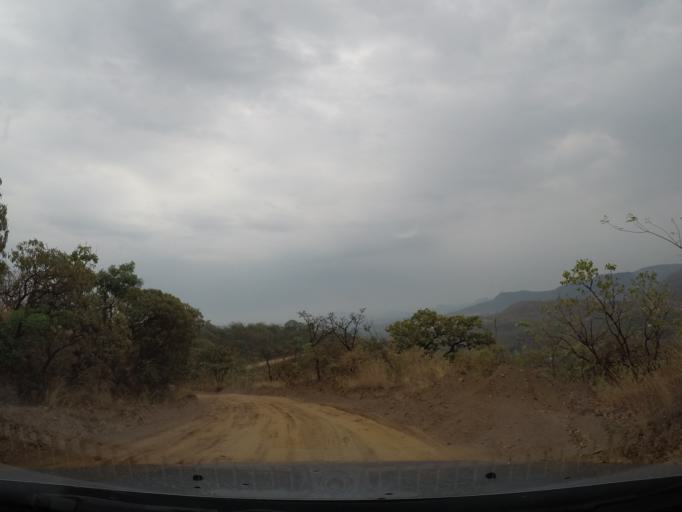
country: BR
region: Goias
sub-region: Pirenopolis
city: Pirenopolis
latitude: -15.8390
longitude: -48.9150
